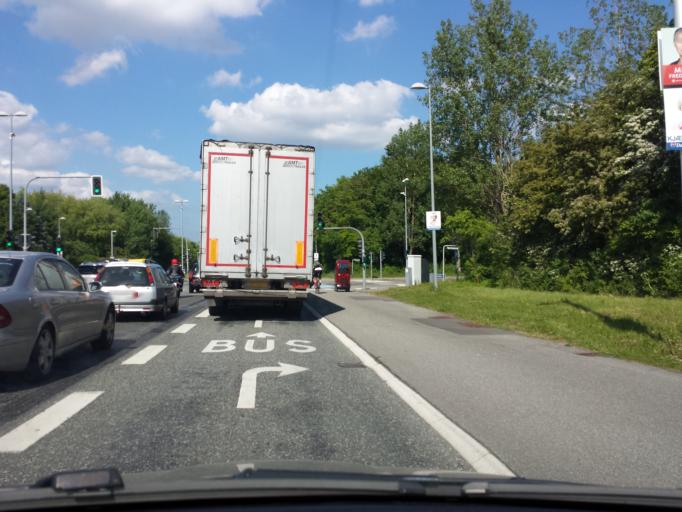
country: DK
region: Capital Region
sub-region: Herlev Kommune
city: Herlev
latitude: 55.6997
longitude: 12.4182
